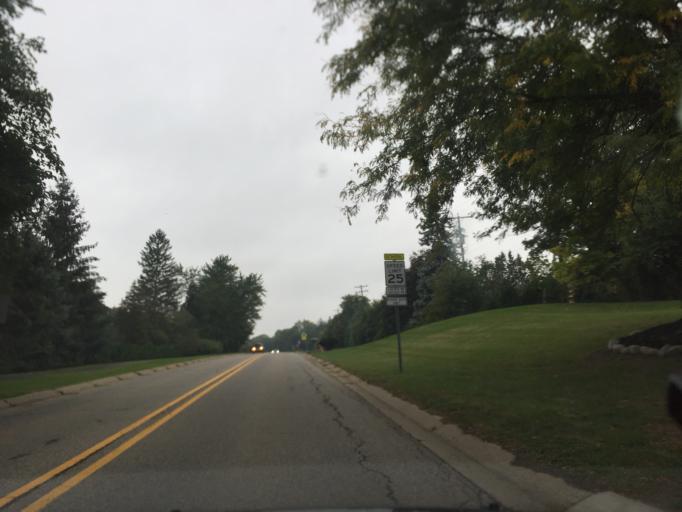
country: US
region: Michigan
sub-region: Oakland County
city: Orchard Lake
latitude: 42.5694
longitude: -83.3294
